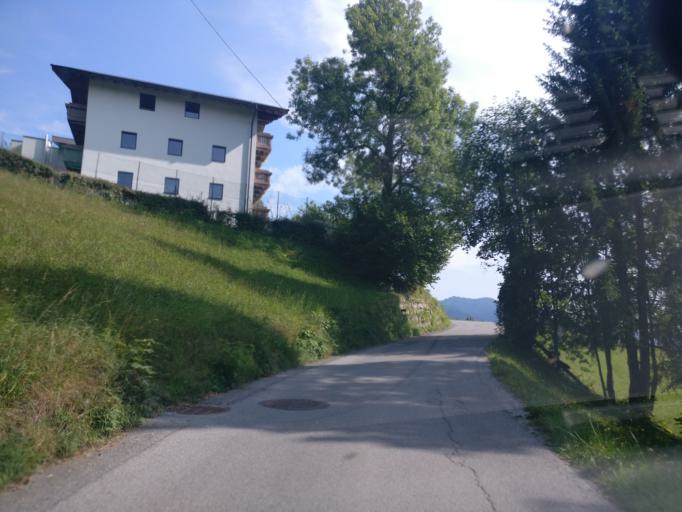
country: AT
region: Salzburg
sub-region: Politischer Bezirk Sankt Johann im Pongau
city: Werfenweng
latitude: 47.4636
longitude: 13.2409
